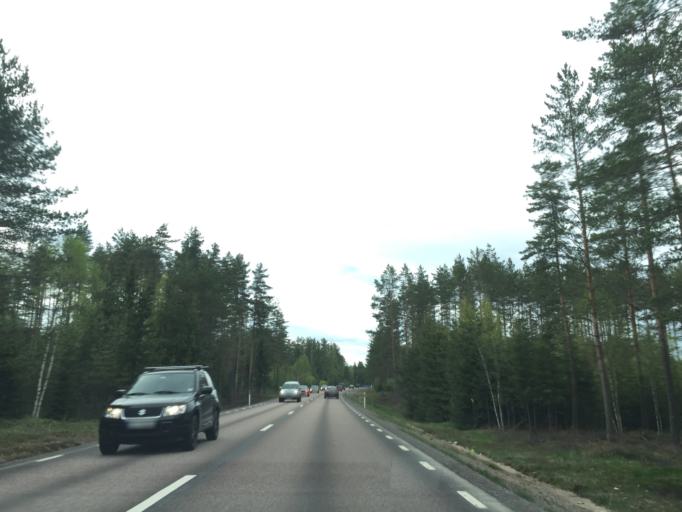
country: SE
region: Vaermland
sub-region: Eda Kommun
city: Charlottenberg
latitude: 59.9074
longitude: 12.2756
